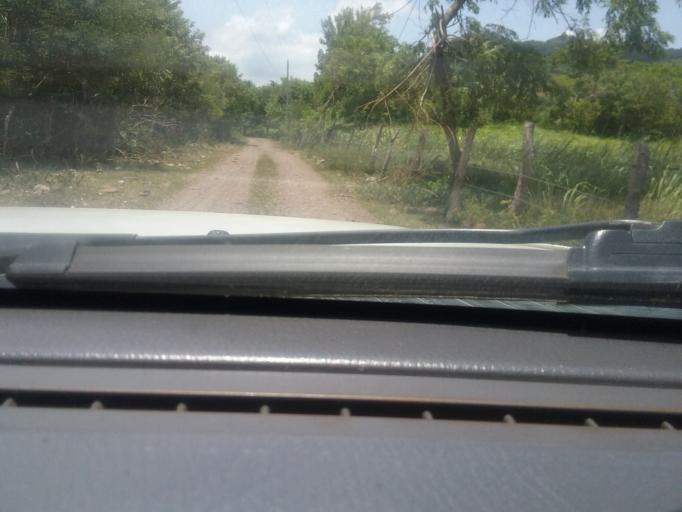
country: NI
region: Matagalpa
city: Terrabona
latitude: 12.6508
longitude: -85.9980
